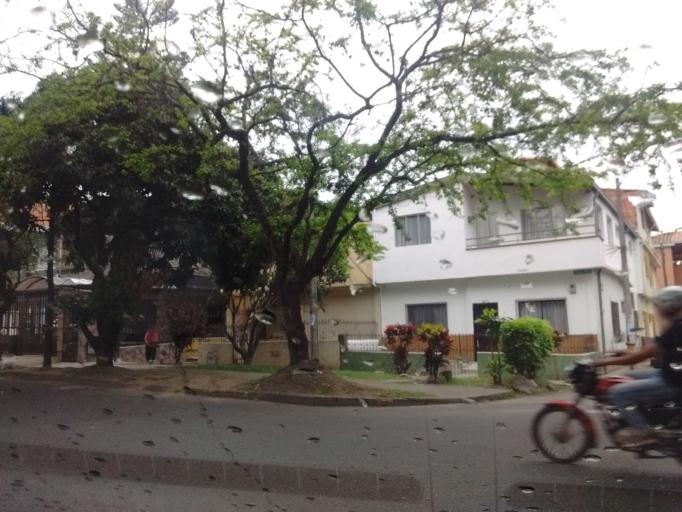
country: CO
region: Antioquia
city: Medellin
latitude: 6.2606
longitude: -75.6020
